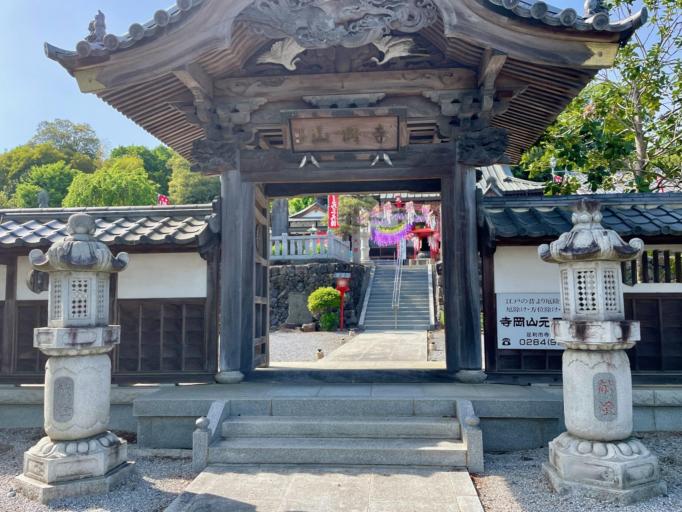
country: JP
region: Tochigi
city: Sano
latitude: 36.3078
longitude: 139.5364
